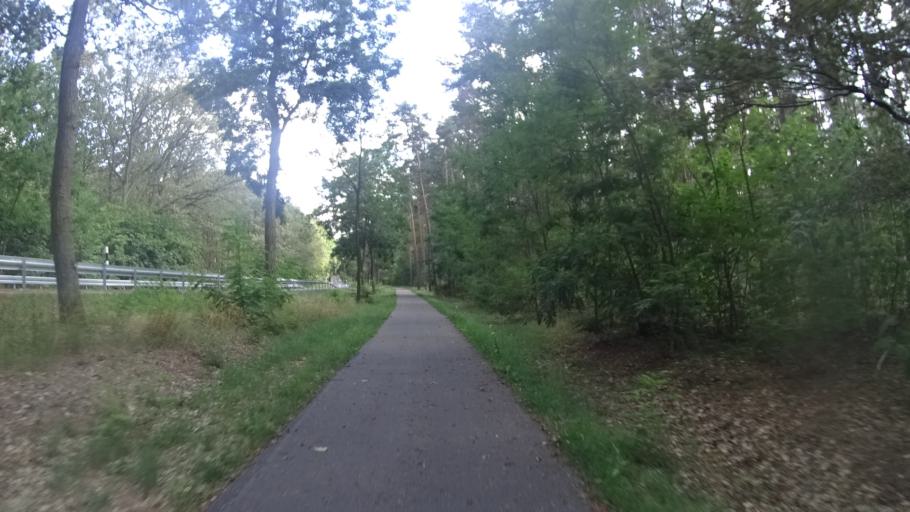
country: DE
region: Brandenburg
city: Rhinow
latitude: 52.7245
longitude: 12.3583
